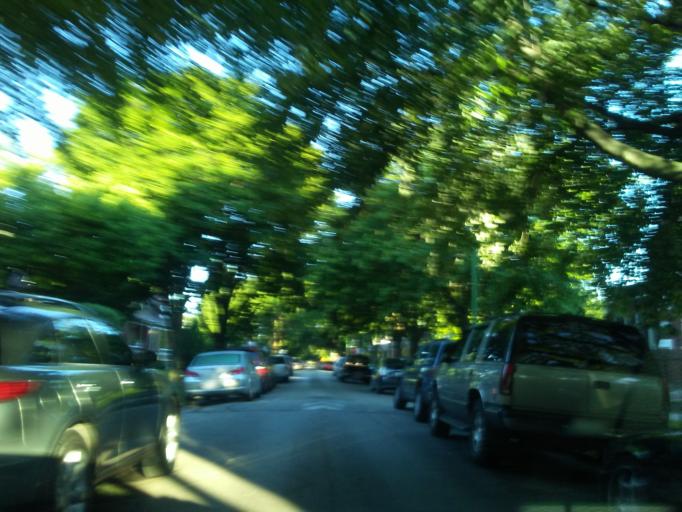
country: US
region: Illinois
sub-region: Cook County
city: Oak Park
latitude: 41.9343
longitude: -87.7482
